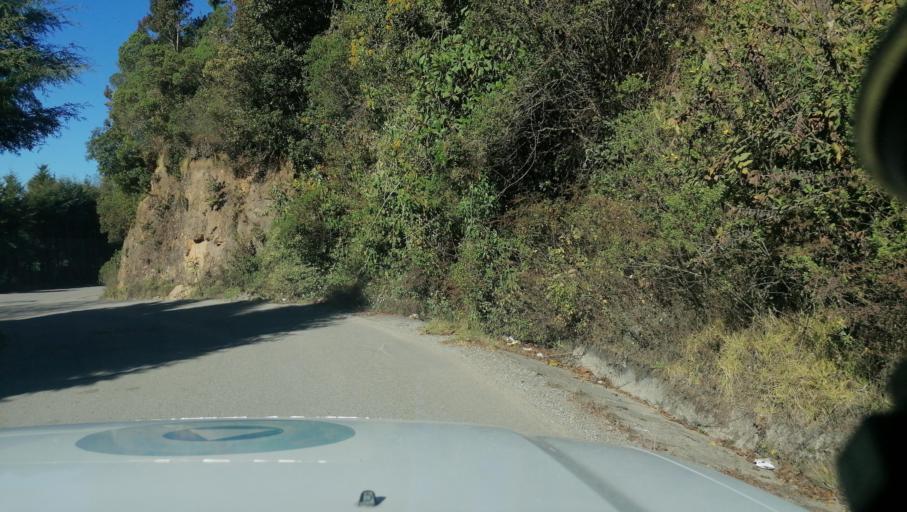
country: MX
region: Chiapas
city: Motozintla de Mendoza
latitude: 15.2665
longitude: -92.2250
